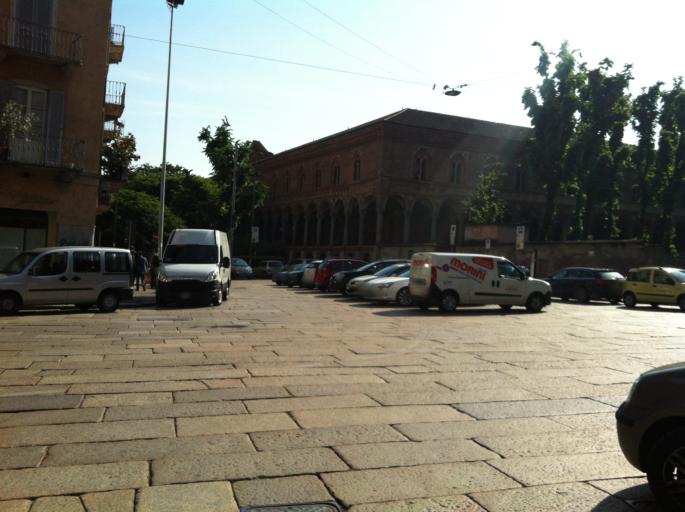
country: IT
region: Lombardy
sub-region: Citta metropolitana di Milano
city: Milano
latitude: 45.4591
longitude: 9.1923
